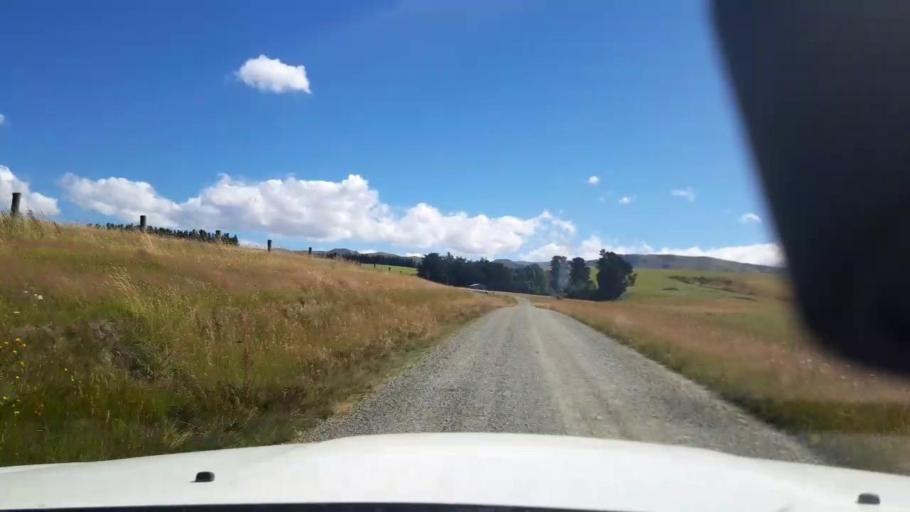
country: NZ
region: Canterbury
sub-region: Timaru District
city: Pleasant Point
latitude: -44.3143
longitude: 170.8907
